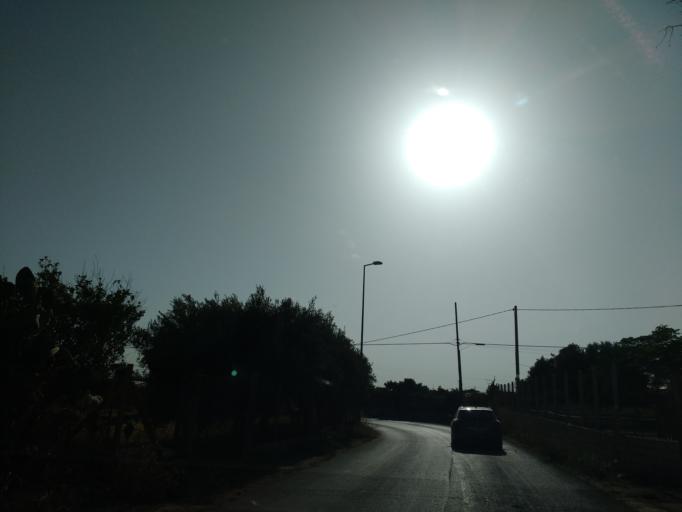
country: IT
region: Sicily
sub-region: Ragusa
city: Cava d'Aliga
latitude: 36.7456
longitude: 14.6786
